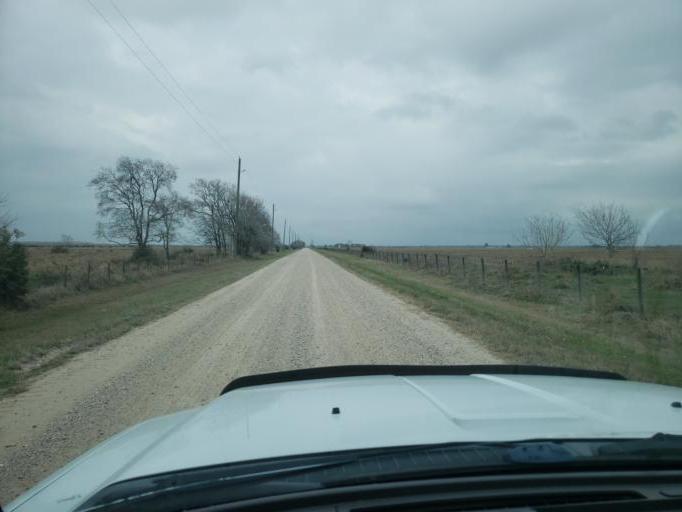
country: US
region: Texas
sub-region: Fort Bend County
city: Needville
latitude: 29.3616
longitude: -95.7330
